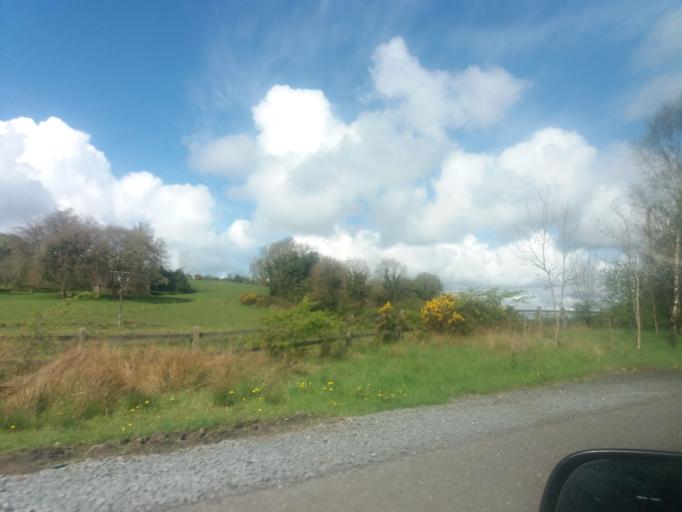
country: IE
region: Ulster
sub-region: An Cabhan
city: Cavan
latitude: 54.0361
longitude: -7.3761
